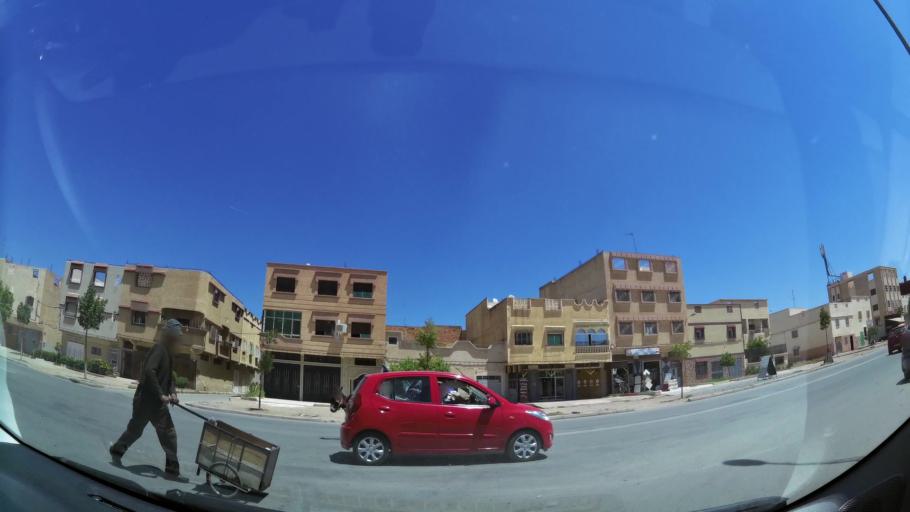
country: MA
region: Oriental
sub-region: Oujda-Angad
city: Oujda
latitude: 34.6770
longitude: -1.8866
